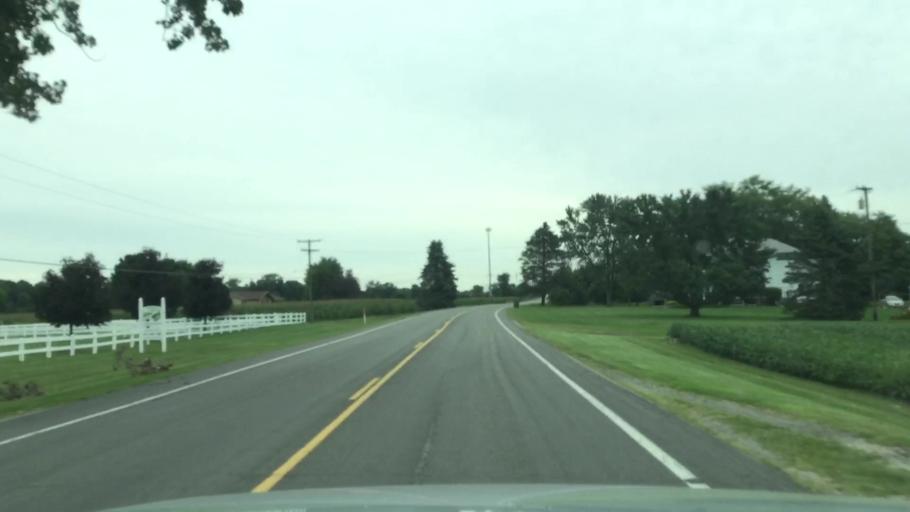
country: US
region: Michigan
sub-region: Washtenaw County
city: Milan
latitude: 42.1288
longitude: -83.6880
